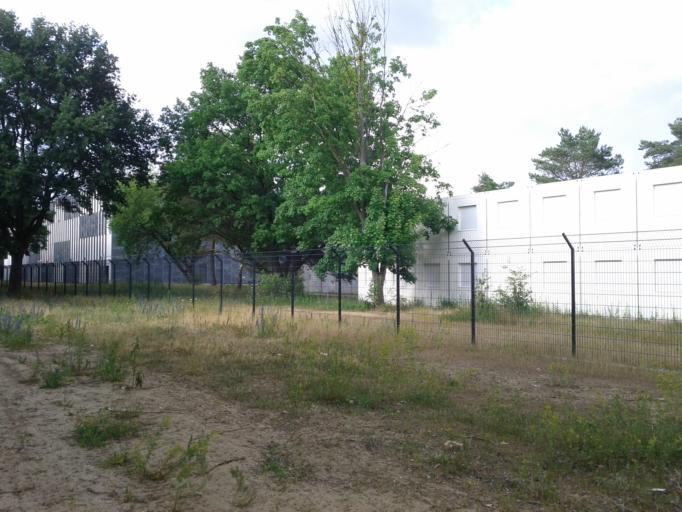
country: DE
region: Berlin
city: Friedrichshagen
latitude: 52.4516
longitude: 13.6123
